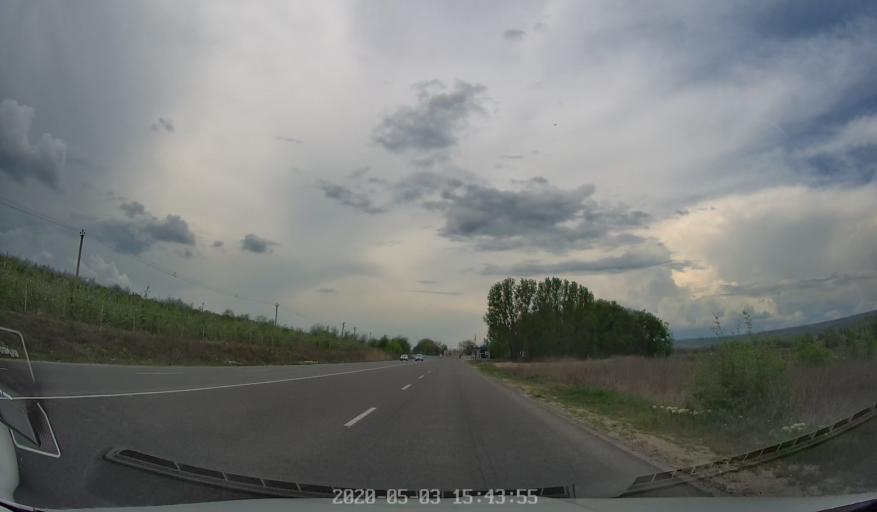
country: MD
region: Straseni
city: Straseni
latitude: 47.1285
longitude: 28.6626
